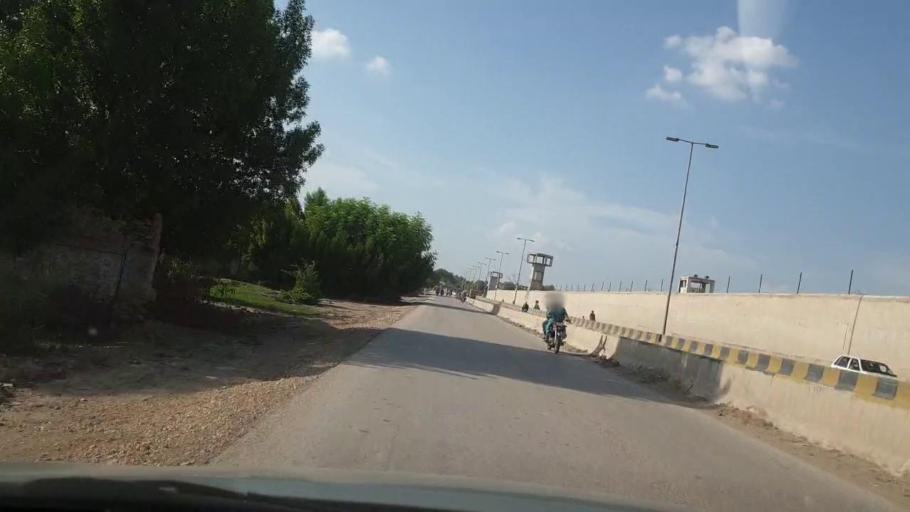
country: PK
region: Sindh
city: Sukkur
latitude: 27.6654
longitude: 68.8466
